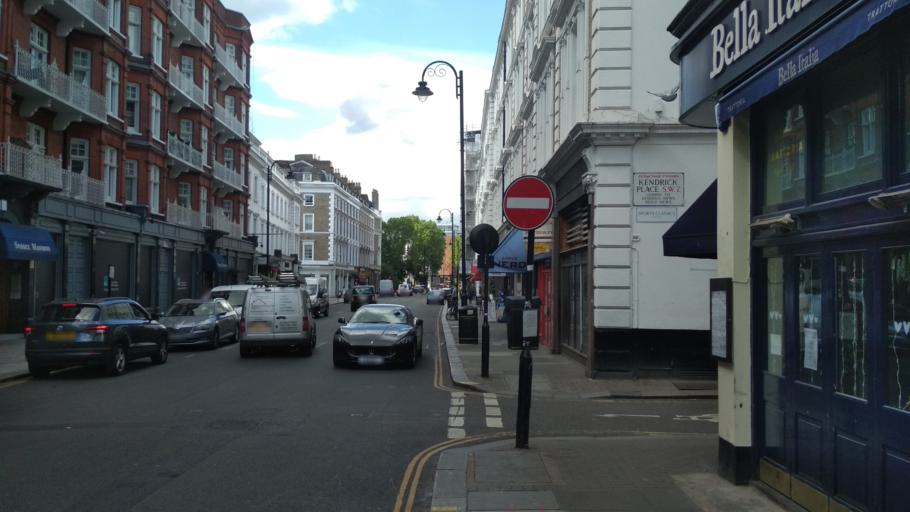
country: GB
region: England
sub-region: Greater London
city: Chelsea
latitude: 51.4931
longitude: -0.1764
